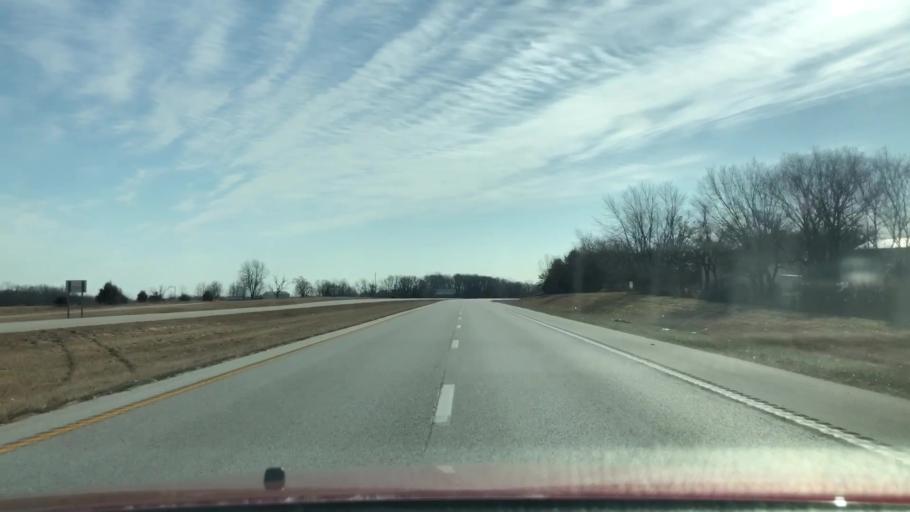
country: US
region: Missouri
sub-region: Webster County
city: Seymour
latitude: 37.1470
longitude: -92.7505
